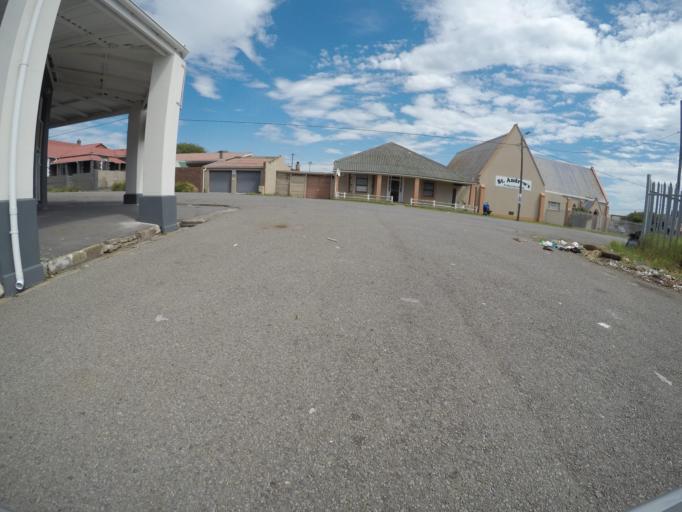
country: ZA
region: Eastern Cape
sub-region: Buffalo City Metropolitan Municipality
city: East London
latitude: -33.0315
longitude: 27.9088
